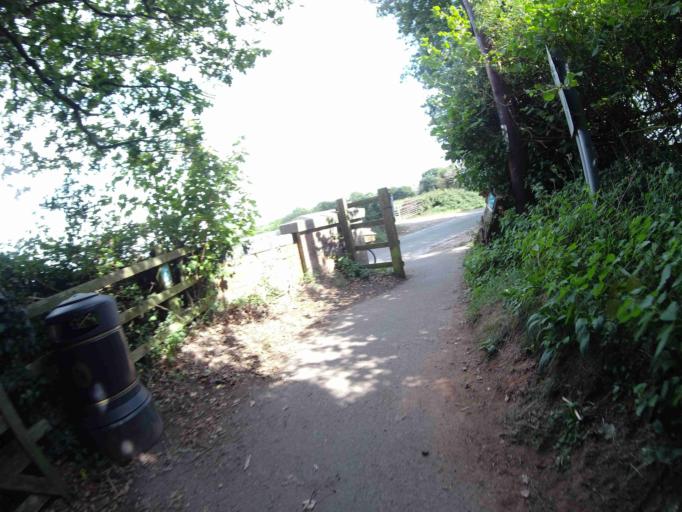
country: GB
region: England
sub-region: Devon
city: Budleigh Salterton
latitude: 50.6390
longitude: -3.3404
